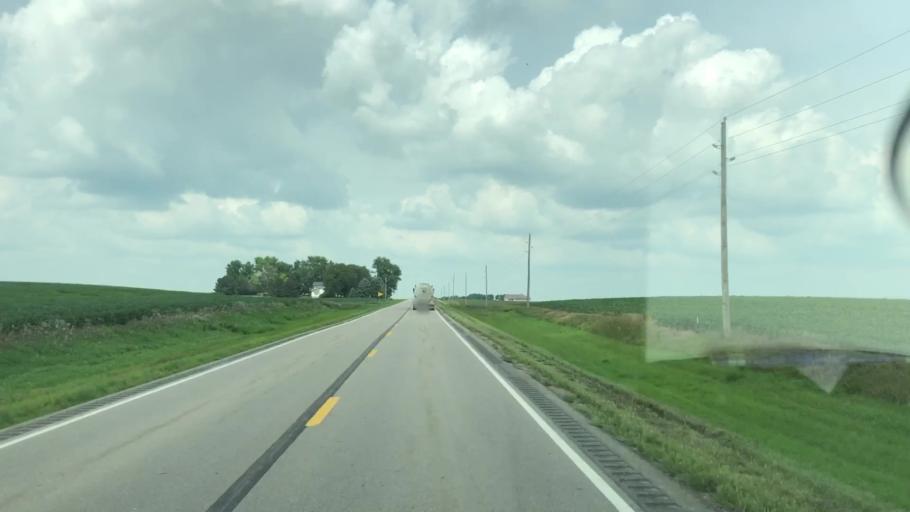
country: US
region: Iowa
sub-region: Plymouth County
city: Remsen
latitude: 42.7874
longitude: -95.9578
